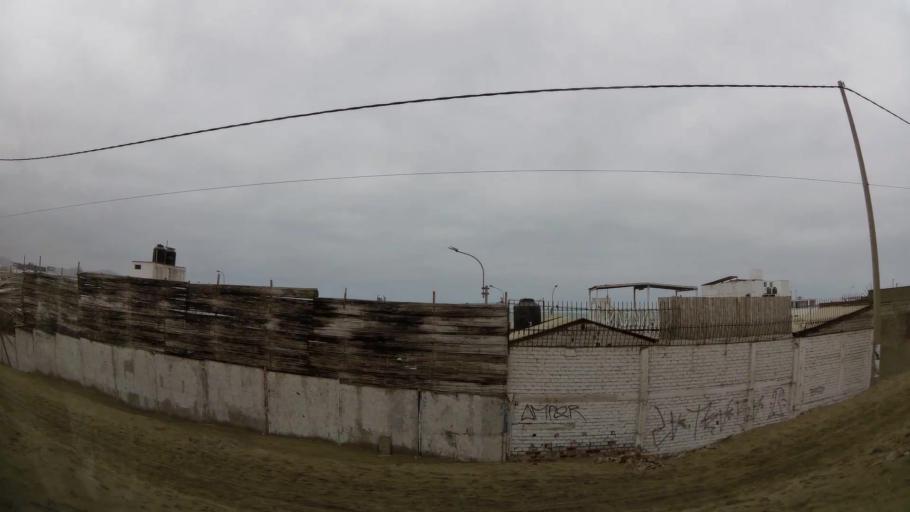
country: PE
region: Lima
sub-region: Lima
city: Punta Hermosa
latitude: -12.3552
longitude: -76.8055
